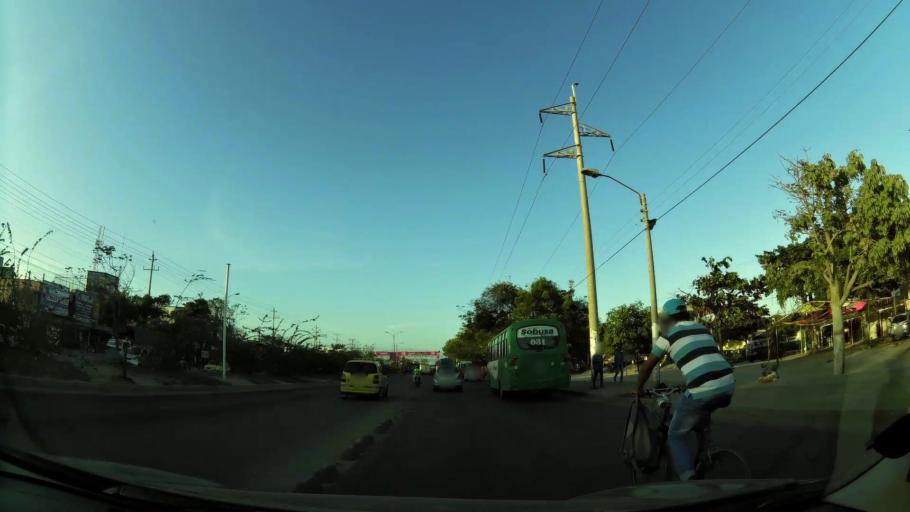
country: CO
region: Atlantico
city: Soledad
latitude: 10.9160
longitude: -74.7990
